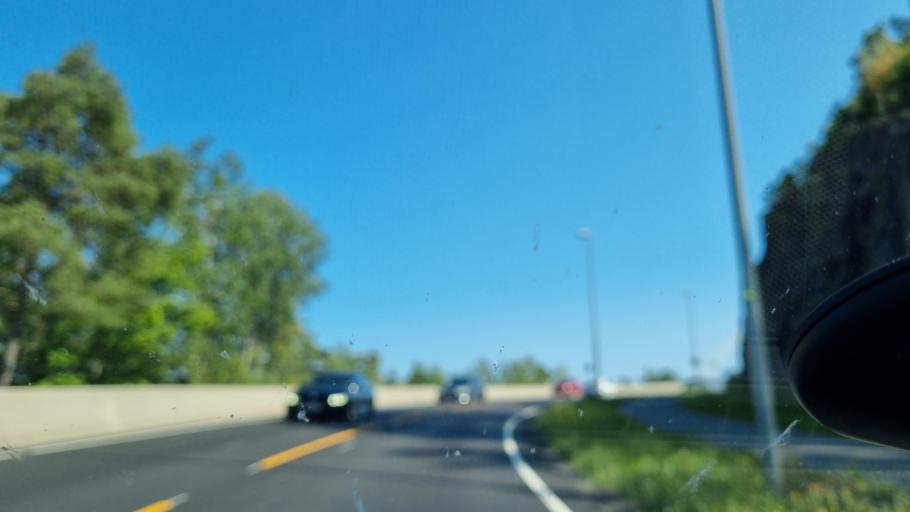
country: NO
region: Aust-Agder
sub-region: Arendal
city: Arendal
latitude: 58.4737
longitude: 8.8205
